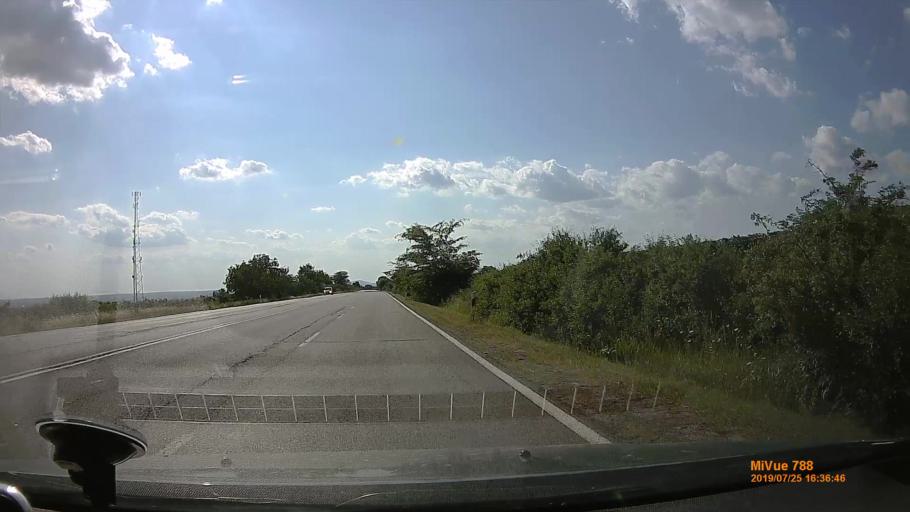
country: HU
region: Heves
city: Abasar
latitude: 47.7702
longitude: 19.9748
